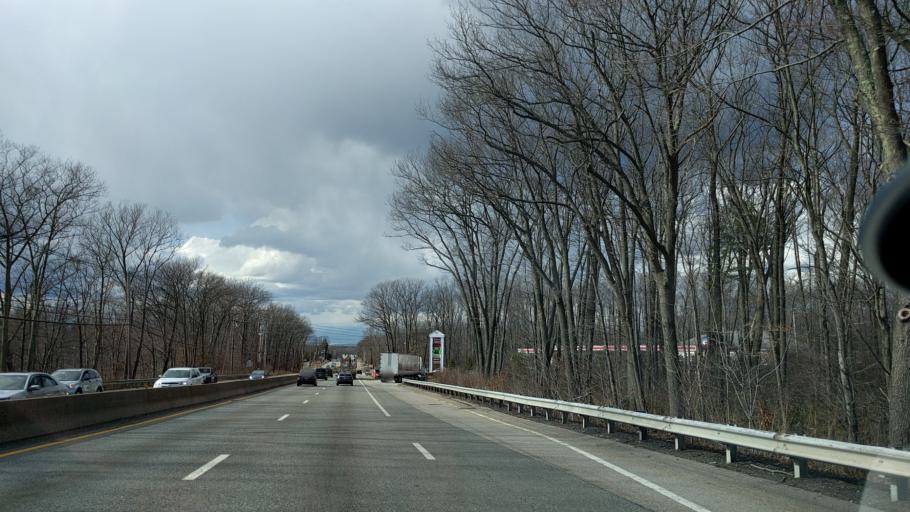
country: US
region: Massachusetts
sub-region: Worcester County
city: Millbury
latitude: 42.1728
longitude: -71.7528
